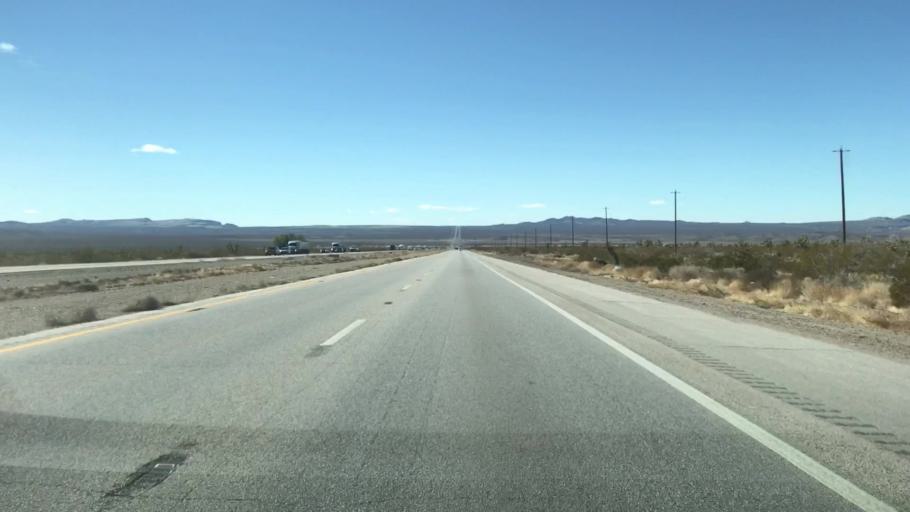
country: US
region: Nevada
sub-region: Clark County
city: Sandy Valley
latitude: 35.4584
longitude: -115.6348
